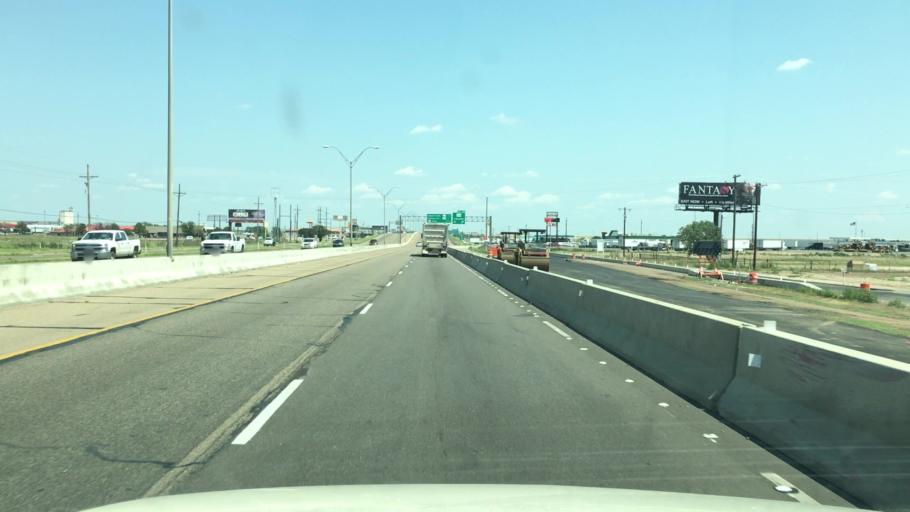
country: US
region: Texas
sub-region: Potter County
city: Amarillo
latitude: 35.1926
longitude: -101.7488
